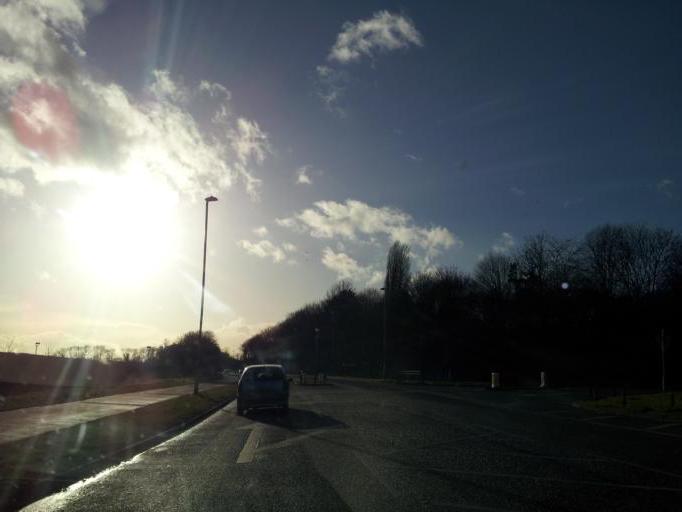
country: GB
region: England
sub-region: Nottinghamshire
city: South Collingham
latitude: 53.0809
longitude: -0.7604
